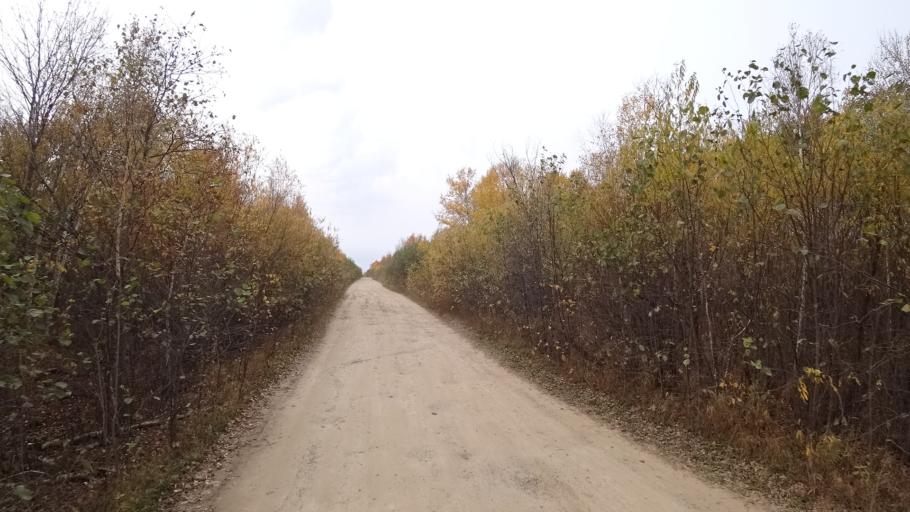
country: RU
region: Khabarovsk Krai
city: Amursk
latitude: 50.1453
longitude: 136.9695
